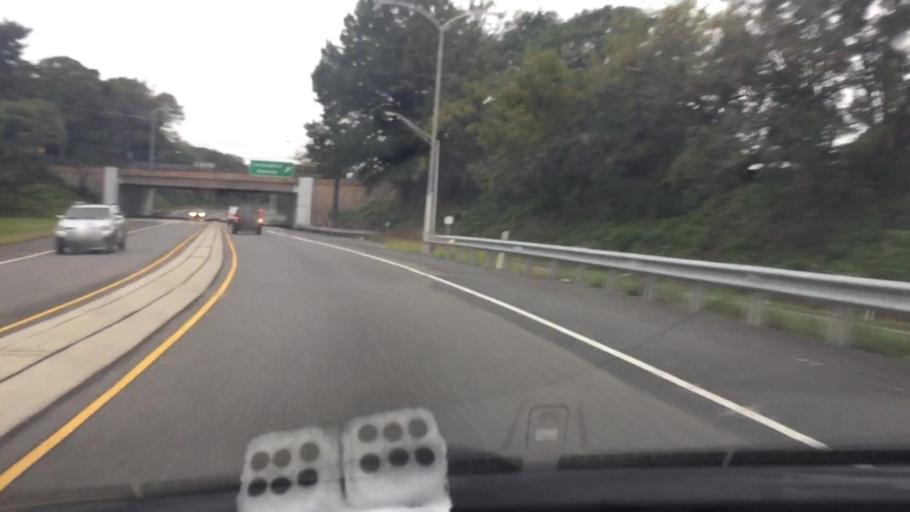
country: US
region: New Jersey
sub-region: Burlington County
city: Riverton
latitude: 40.0487
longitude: -75.0005
